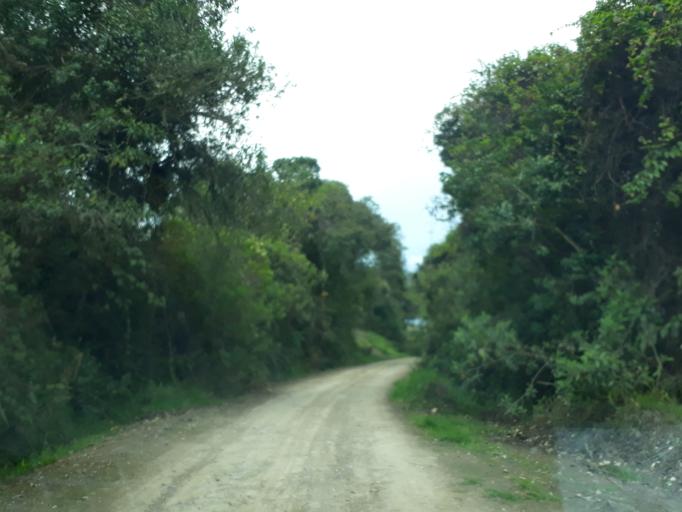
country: CO
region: Cundinamarca
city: Macheta
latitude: 5.0989
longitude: -73.5475
